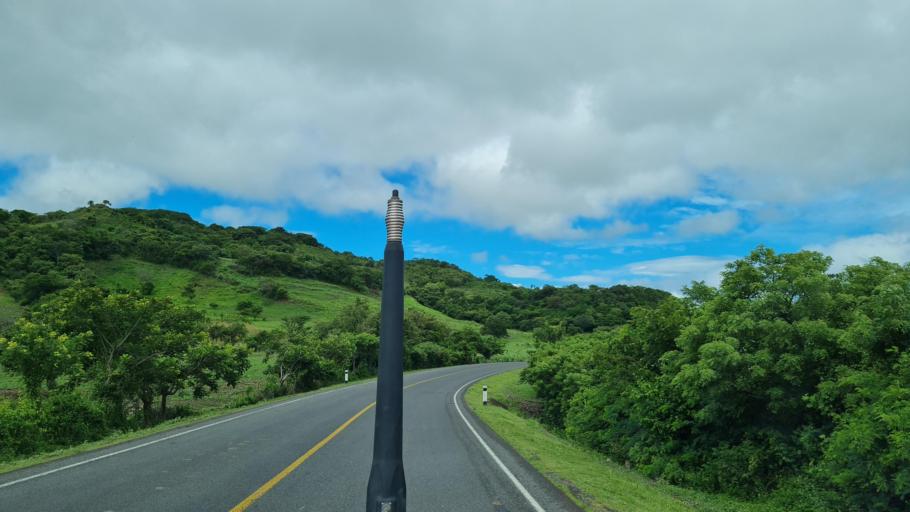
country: NI
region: Matagalpa
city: Terrabona
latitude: 12.5829
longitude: -85.9743
